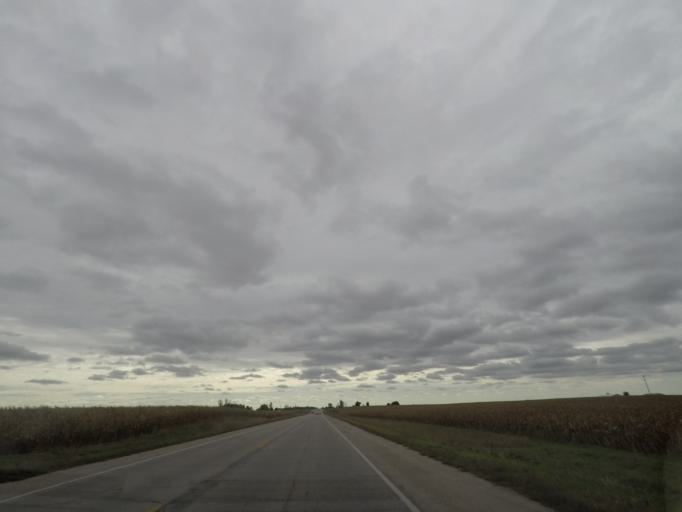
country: US
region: Iowa
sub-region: Story County
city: Nevada
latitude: 42.0135
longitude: -93.3094
